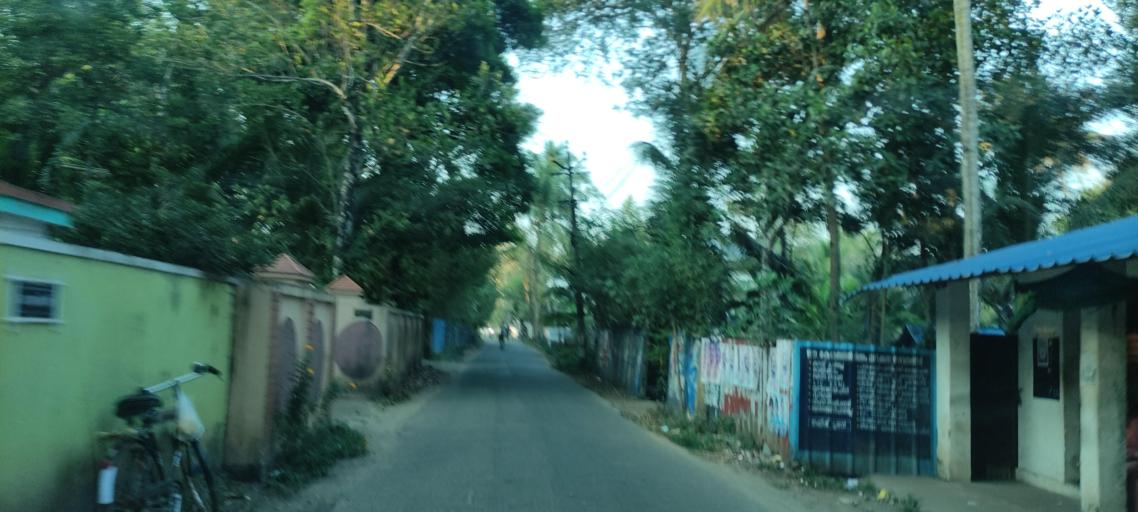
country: IN
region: Kerala
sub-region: Alappuzha
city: Kutiatodu
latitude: 9.7818
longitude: 76.3247
